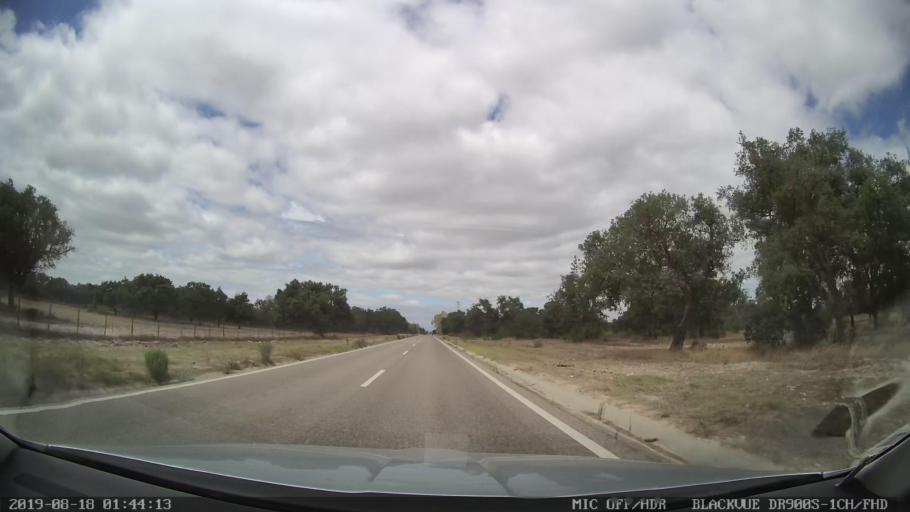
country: PT
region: Santarem
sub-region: Benavente
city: Poceirao
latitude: 38.9018
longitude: -8.7565
